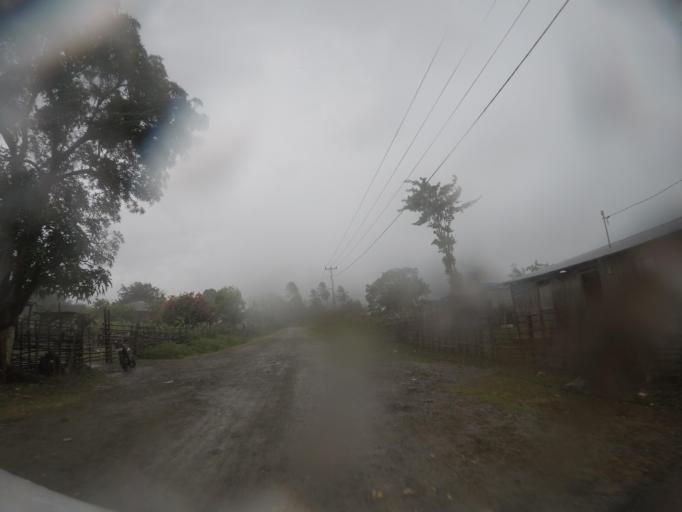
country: TL
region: Bobonaro
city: Maliana
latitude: -8.8558
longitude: 125.0994
